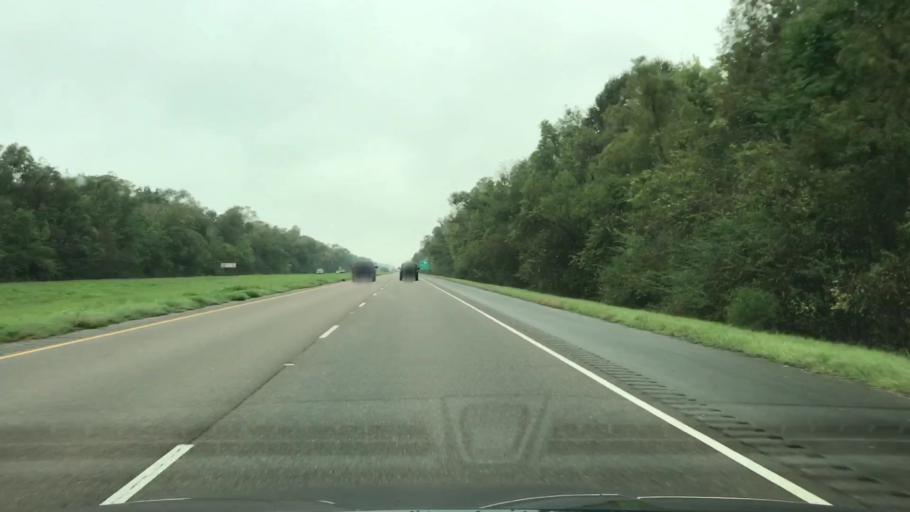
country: US
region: Louisiana
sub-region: Terrebonne Parish
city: Gray
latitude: 29.6845
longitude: -90.7321
